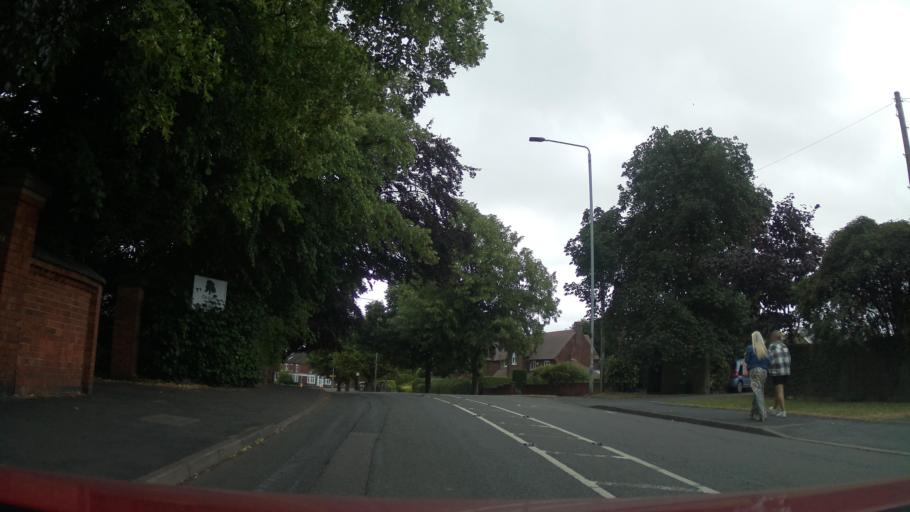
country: GB
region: England
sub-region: Leicestershire
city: Ashby de la Zouch
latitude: 52.7486
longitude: -1.4809
